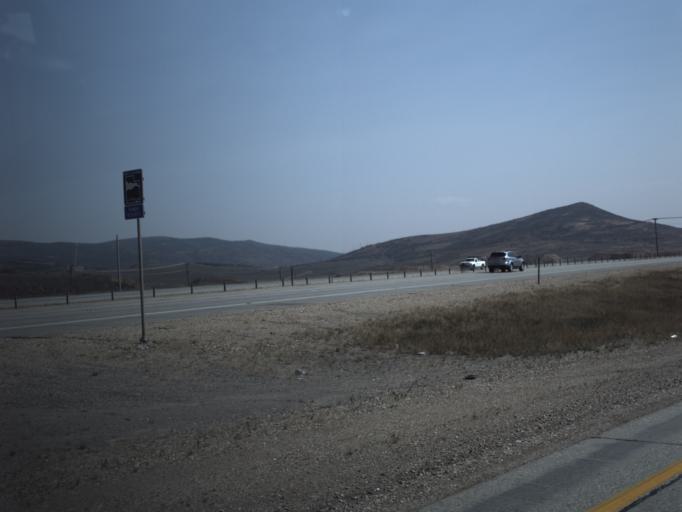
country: US
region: Utah
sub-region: Summit County
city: Park City
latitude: 40.6858
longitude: -111.4641
